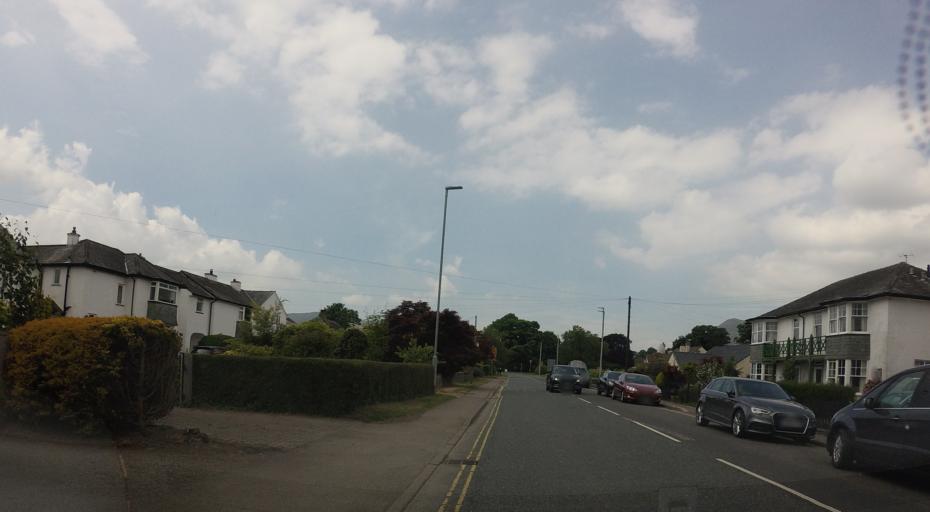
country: GB
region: England
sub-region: Cumbria
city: Keswick
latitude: 54.6056
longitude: -3.1466
